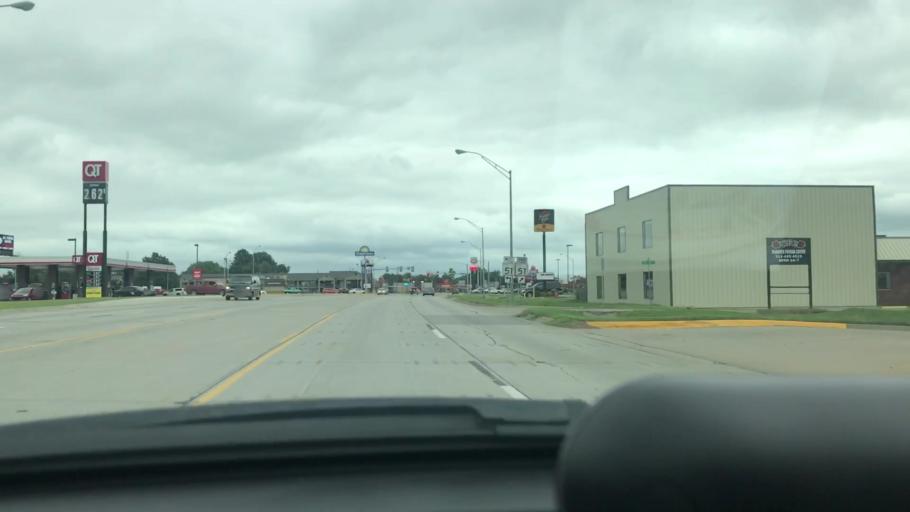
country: US
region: Oklahoma
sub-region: Wagoner County
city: Wagoner
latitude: 35.9573
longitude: -95.3952
